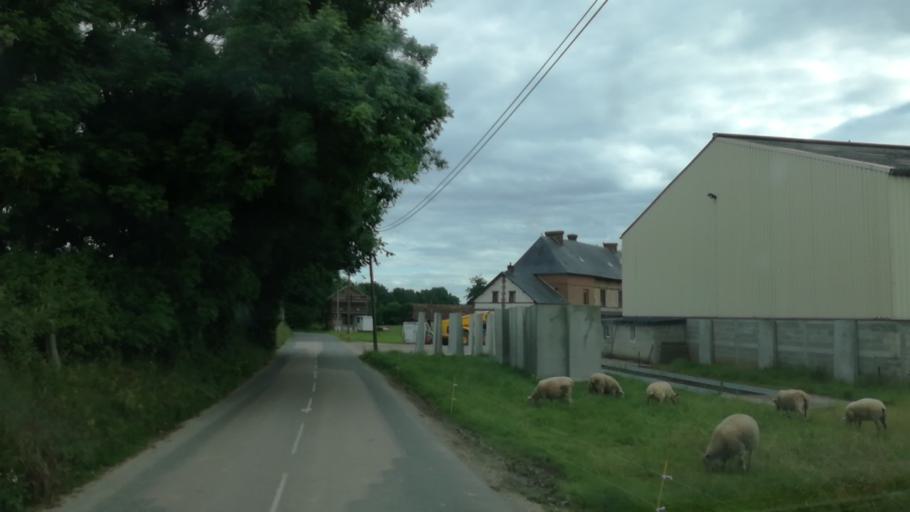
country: FR
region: Haute-Normandie
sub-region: Departement de l'Eure
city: Bourg-Achard
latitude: 49.3007
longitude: 0.8029
